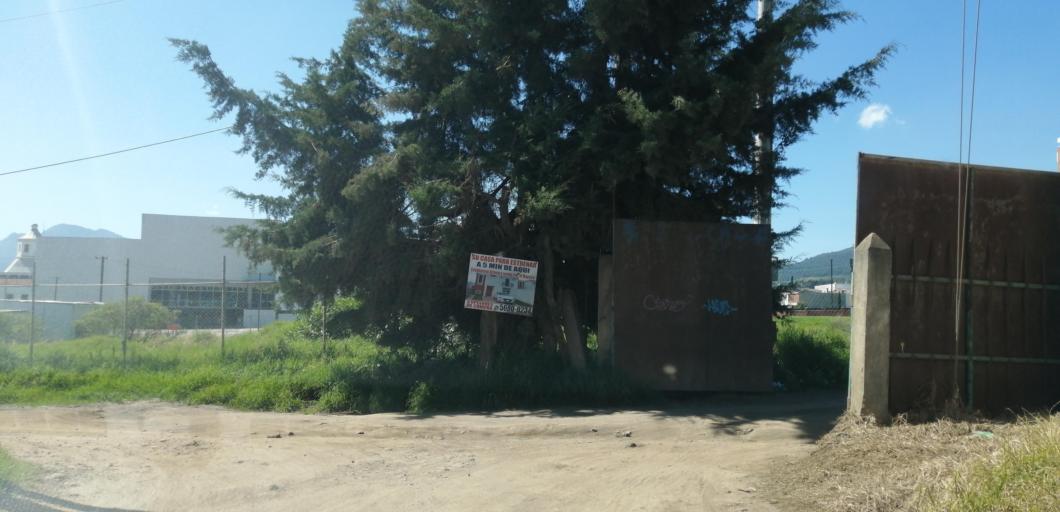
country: GT
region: Quetzaltenango
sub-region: Municipio de La Esperanza
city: La Esperanza
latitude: 14.8647
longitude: -91.5507
